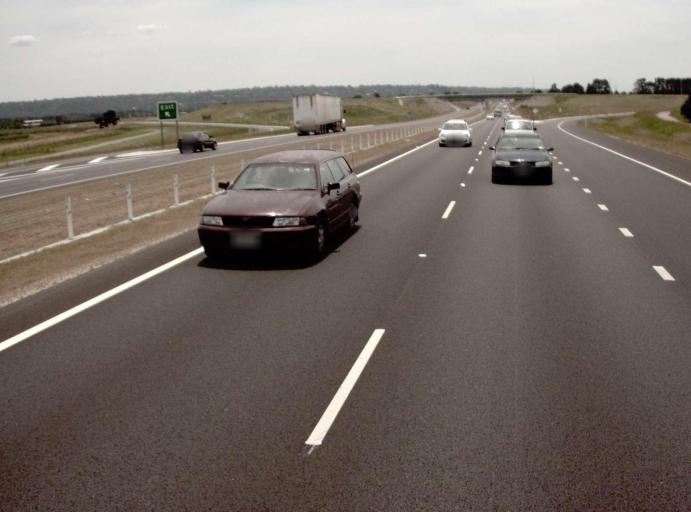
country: AU
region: Victoria
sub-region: Mornington Peninsula
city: Moorooduc
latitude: -38.2377
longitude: 145.1241
